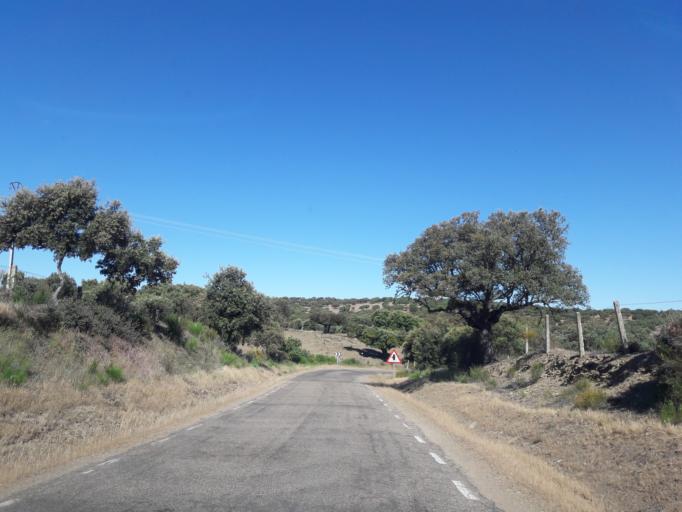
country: ES
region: Castille and Leon
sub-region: Provincia de Salamanca
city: Juzbado
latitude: 41.0641
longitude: -5.8978
